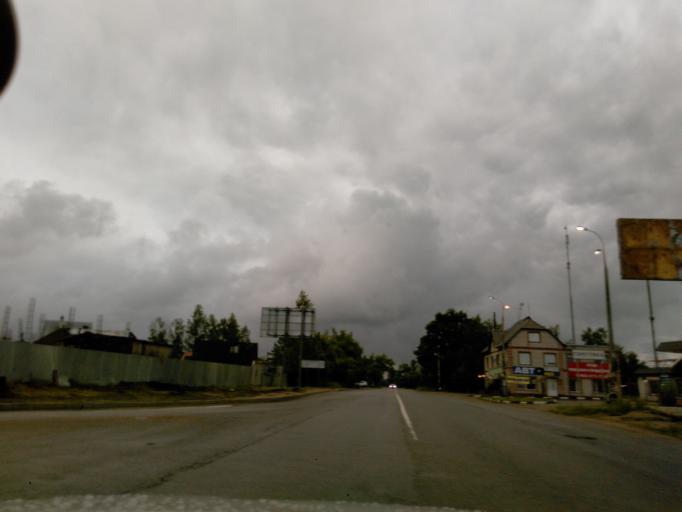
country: RU
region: Moskovskaya
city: Andreyevka
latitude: 55.9624
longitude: 37.1052
